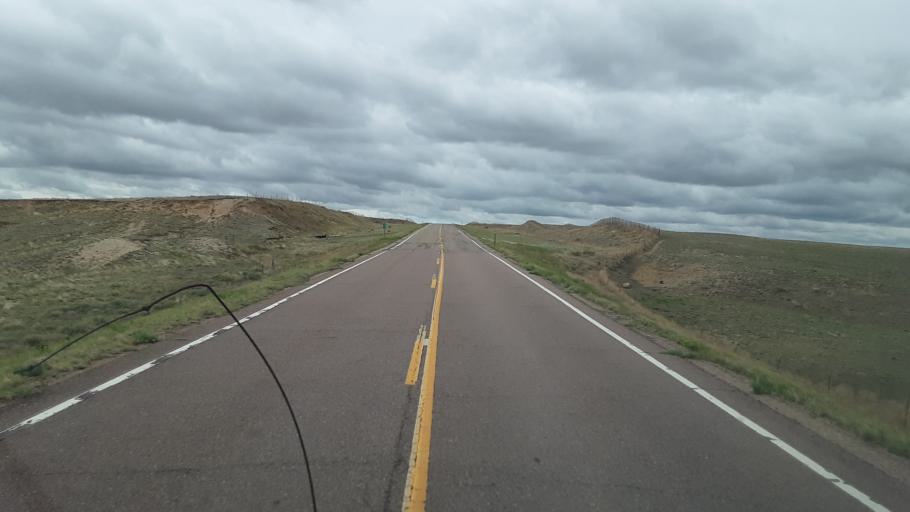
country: US
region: Colorado
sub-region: Lincoln County
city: Limon
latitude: 38.8393
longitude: -103.9071
